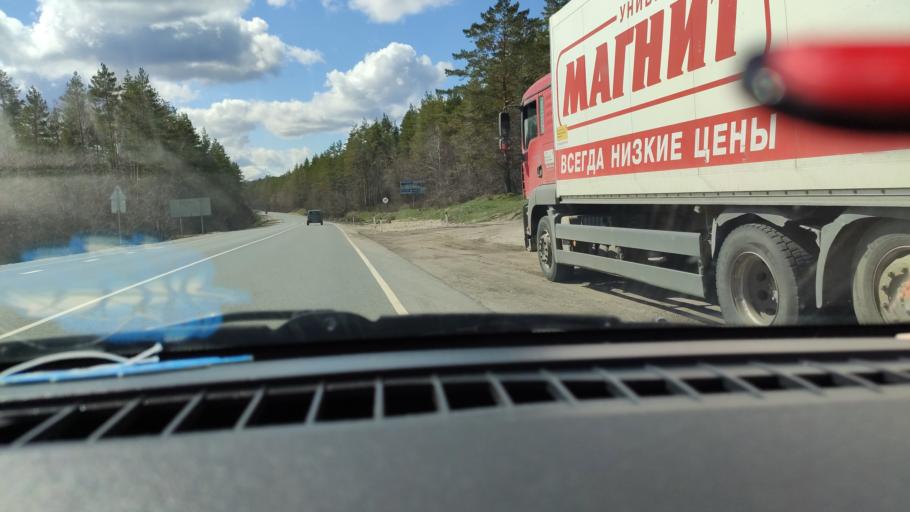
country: RU
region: Saratov
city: Khvalynsk
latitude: 52.5191
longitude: 48.0184
